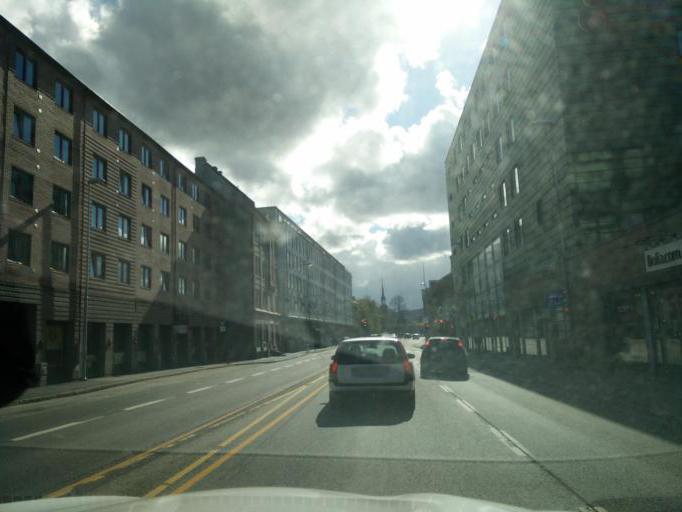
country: NO
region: Sor-Trondelag
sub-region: Trondheim
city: Trondheim
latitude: 63.4348
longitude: 10.4154
